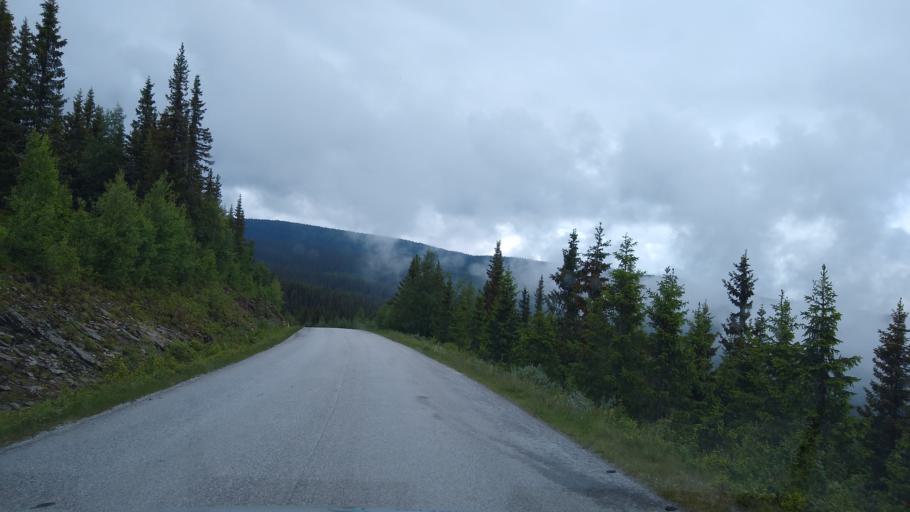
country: NO
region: Oppland
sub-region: Ringebu
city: Ringebu
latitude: 61.4828
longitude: 10.1216
